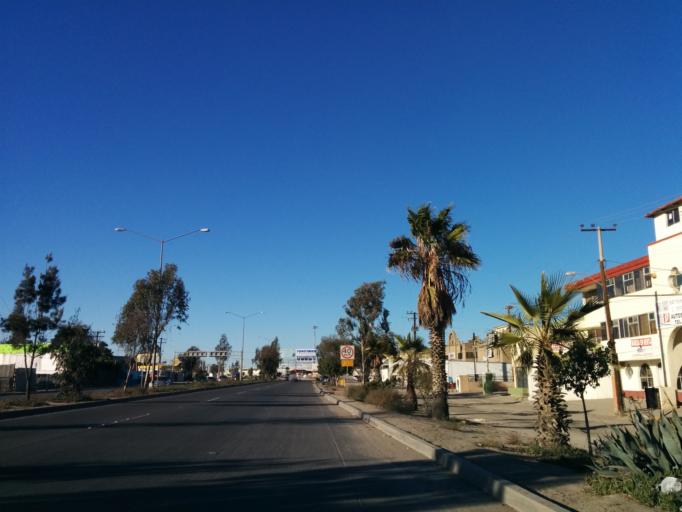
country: MX
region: Baja California
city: Tijuana
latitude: 32.5450
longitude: -116.9477
